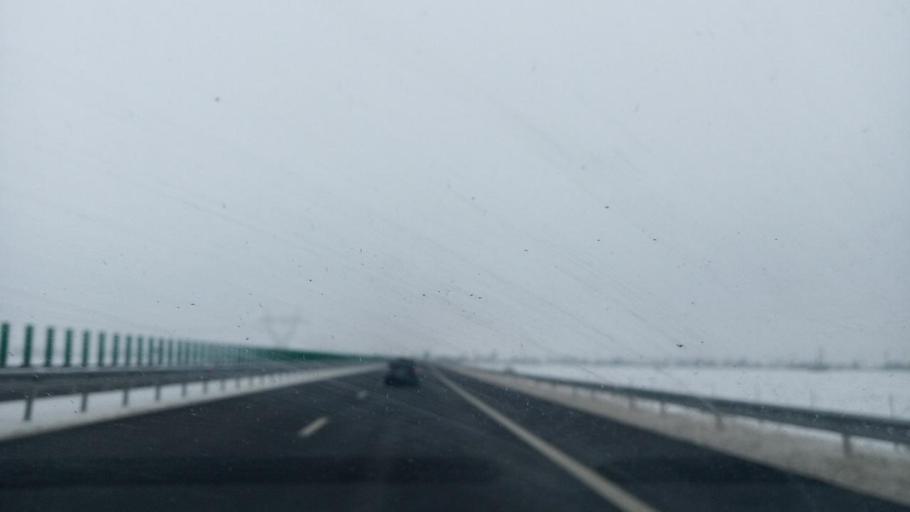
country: RO
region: Bacau
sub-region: Comuna Letea Veche
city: Holt
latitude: 46.5756
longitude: 26.9646
